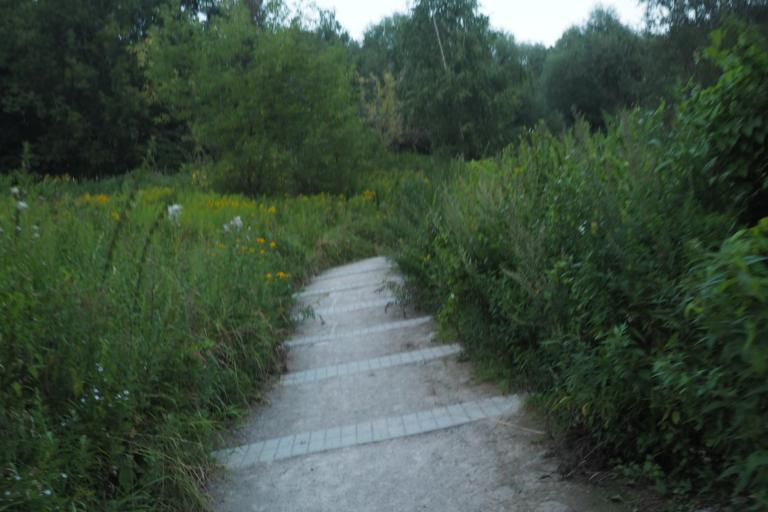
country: RU
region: Moscow
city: Orekhovo-Borisovo Severnoye
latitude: 55.6066
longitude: 37.6958
